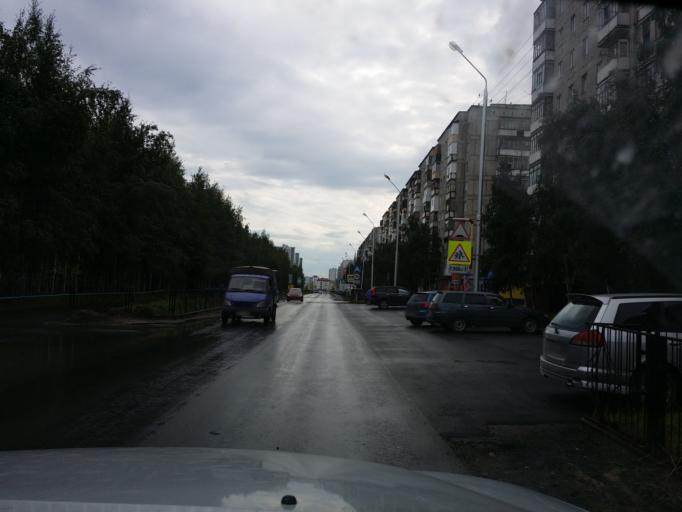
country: RU
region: Khanty-Mansiyskiy Avtonomnyy Okrug
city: Nizhnevartovsk
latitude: 60.9455
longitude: 76.5955
